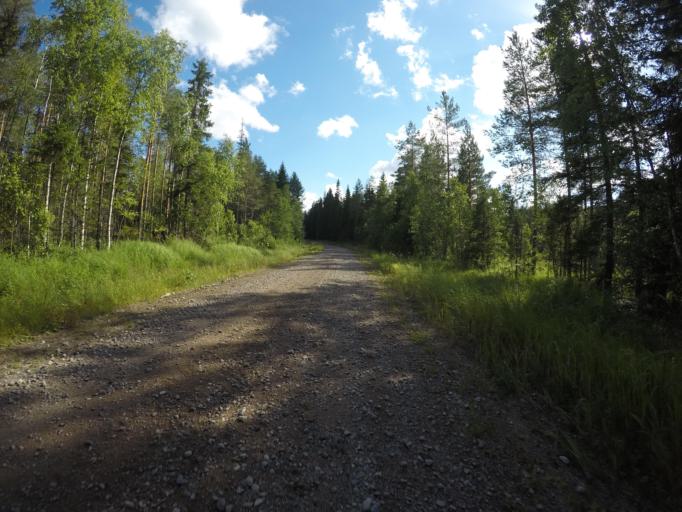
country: SE
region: Dalarna
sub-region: Ludvika Kommun
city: Abborrberget
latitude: 60.0077
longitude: 14.6095
